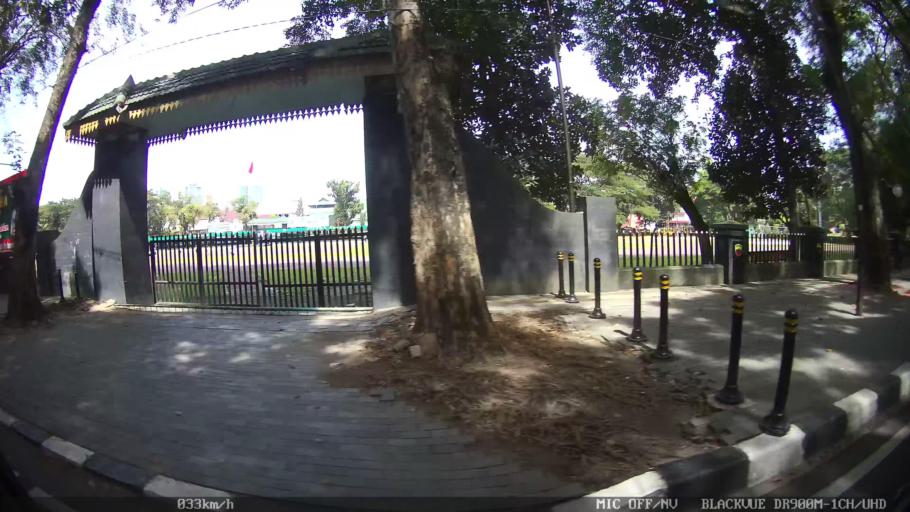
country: ID
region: North Sumatra
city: Medan
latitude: 3.5887
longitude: 98.6737
